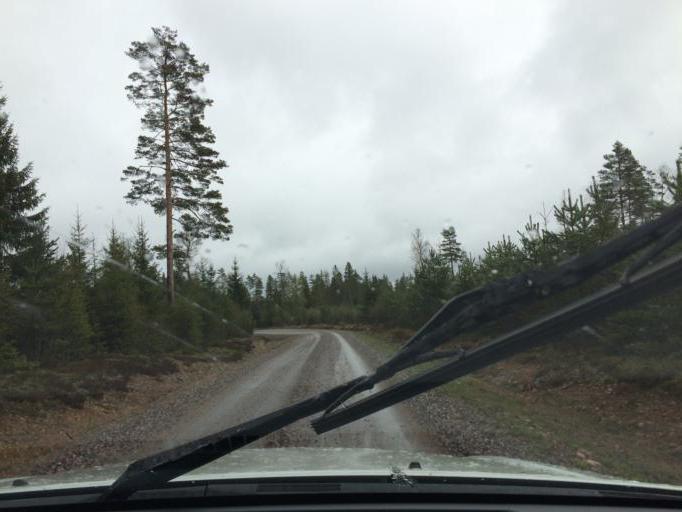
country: SE
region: OErebro
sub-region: Hallefors Kommun
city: Haellefors
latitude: 60.0342
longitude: 14.5358
